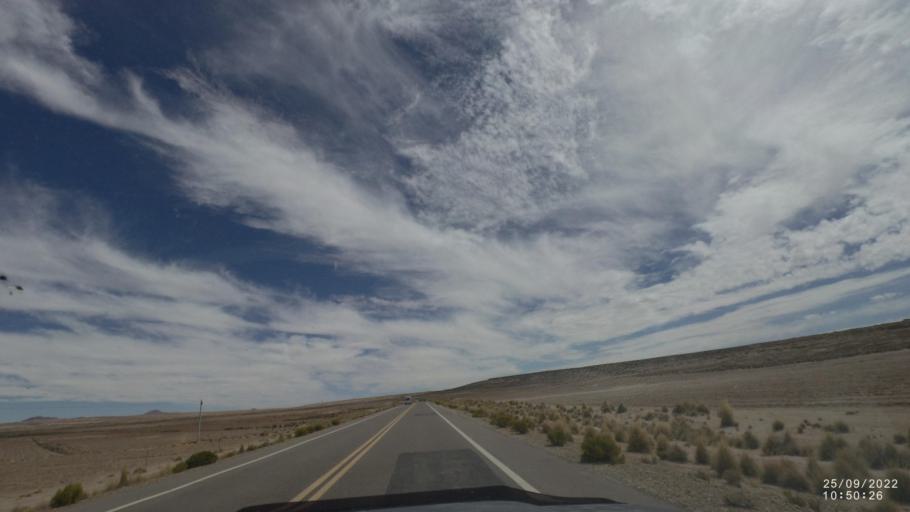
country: BO
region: Oruro
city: Challapata
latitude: -19.5757
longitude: -66.8378
